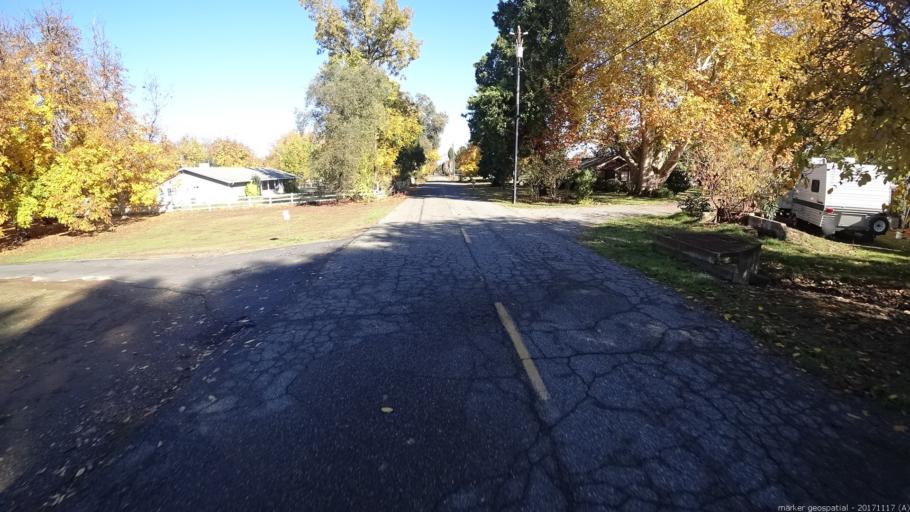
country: US
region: California
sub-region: Shasta County
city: Anderson
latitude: 40.4499
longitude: -122.2371
